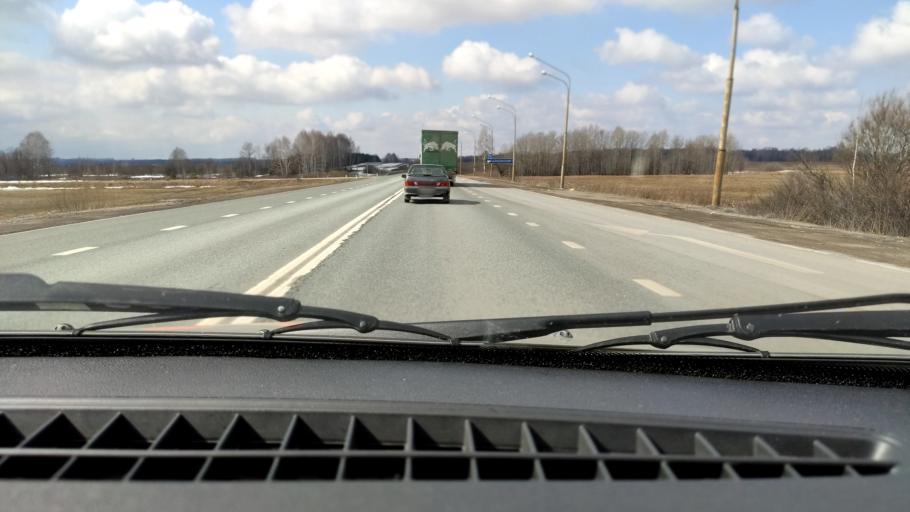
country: RU
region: Bashkortostan
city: Kudeyevskiy
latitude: 54.8169
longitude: 56.7324
